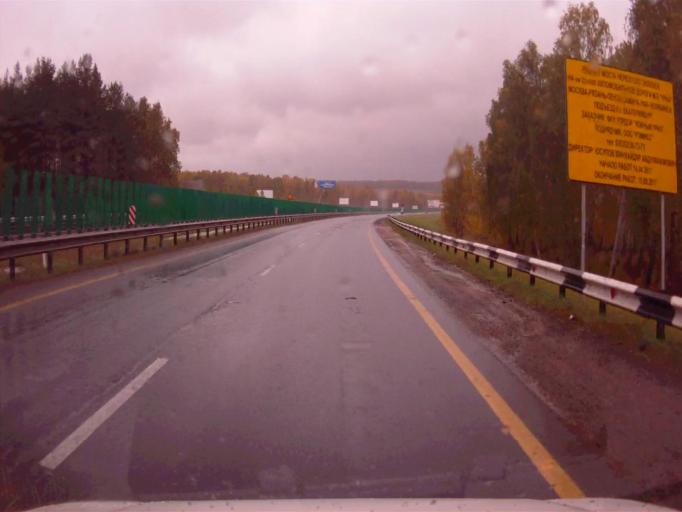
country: RU
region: Chelyabinsk
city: Dolgoderevenskoye
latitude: 55.3397
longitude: 61.3068
